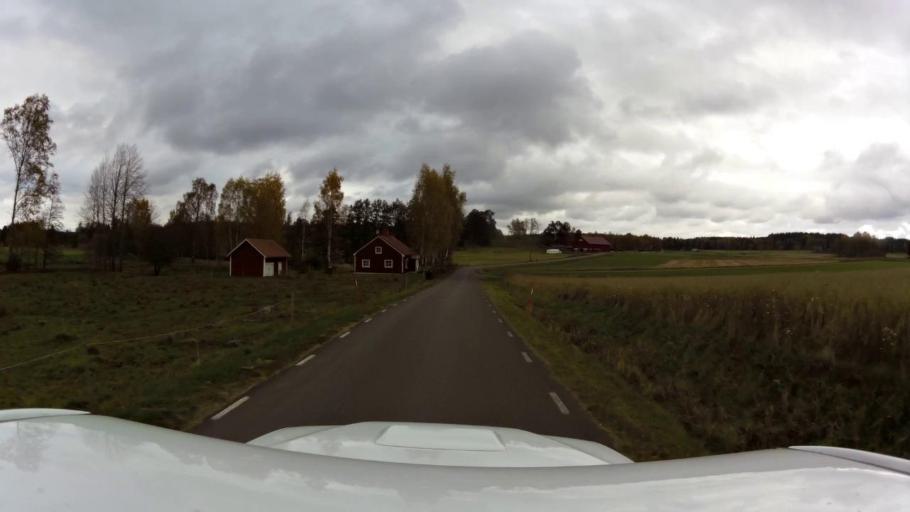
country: SE
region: OEstergoetland
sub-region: Motala Kommun
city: Borensberg
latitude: 58.5668
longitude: 15.3883
